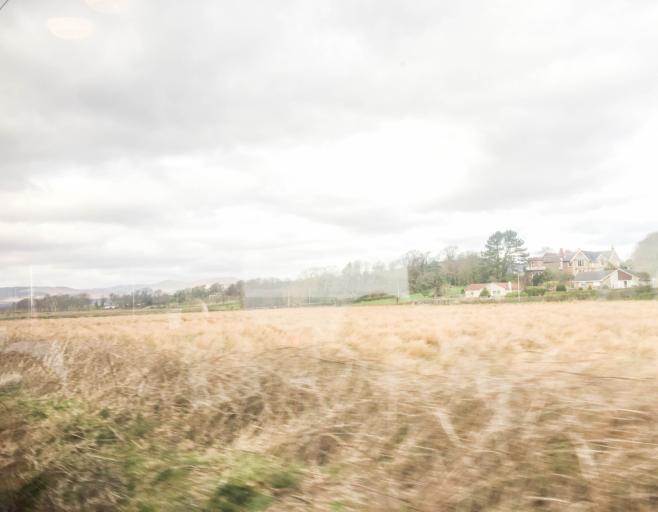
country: GB
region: Scotland
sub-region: Inverclyde
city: Port Glasgow
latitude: 55.9643
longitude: -4.6731
